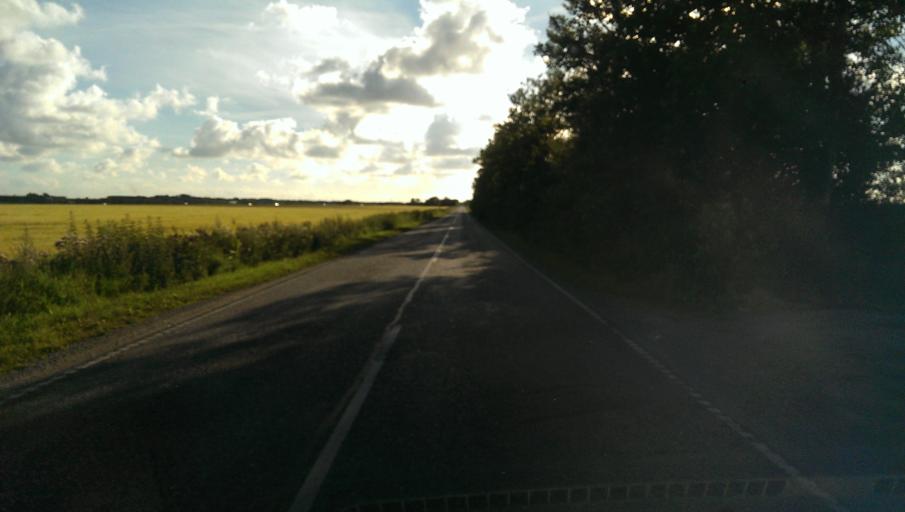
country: DK
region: South Denmark
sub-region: Esbjerg Kommune
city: Tjaereborg
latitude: 55.5208
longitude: 8.5427
